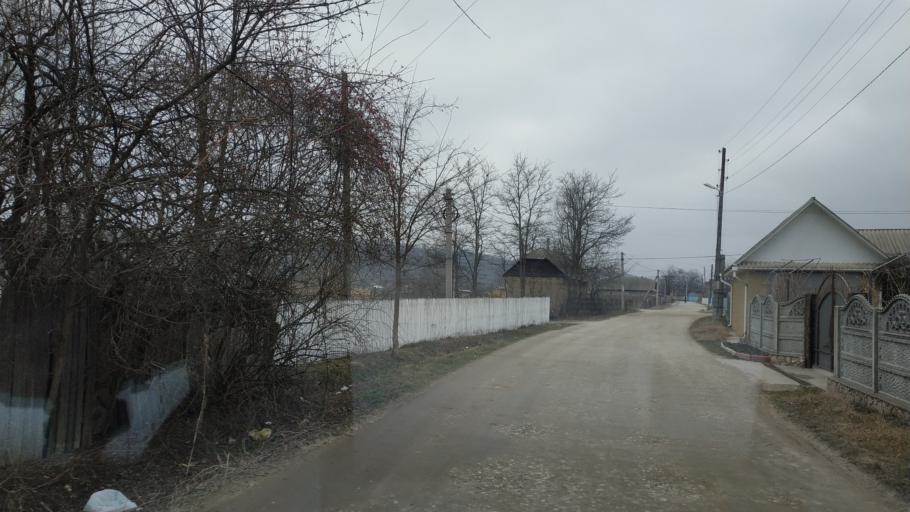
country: MD
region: Hincesti
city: Hincesti
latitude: 46.8838
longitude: 28.4068
